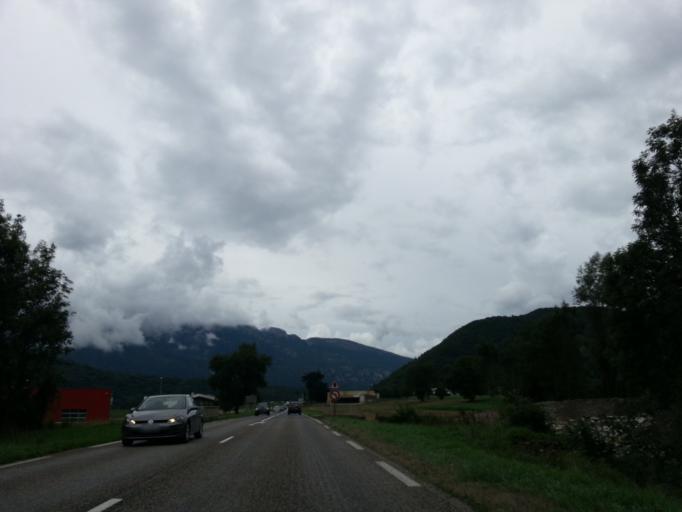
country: FR
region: Rhone-Alpes
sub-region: Departement de la Haute-Savoie
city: Faverges
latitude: 45.7604
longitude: 6.2611
